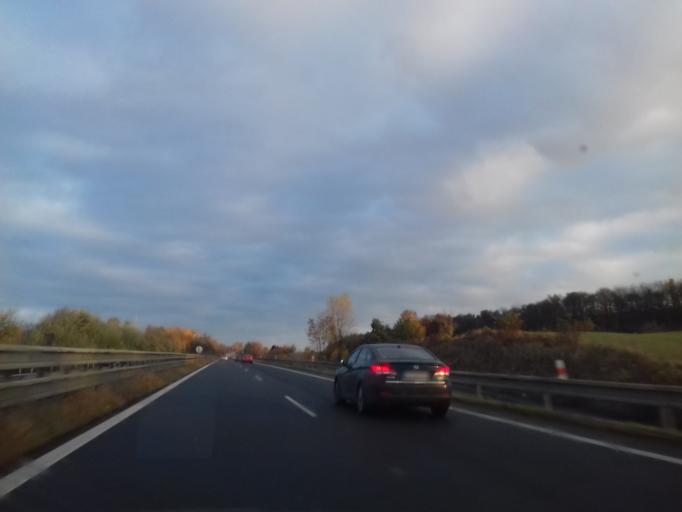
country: CZ
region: Olomoucky
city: Smrzice
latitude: 49.4956
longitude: 17.1417
